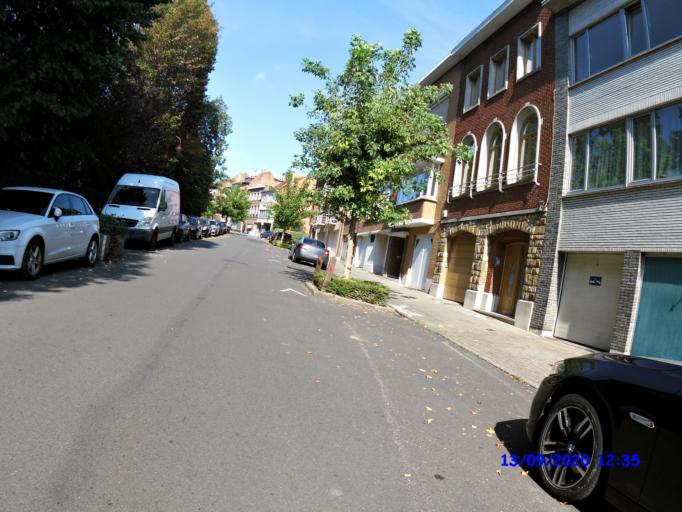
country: BE
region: Flanders
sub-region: Provincie Vlaams-Brabant
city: Wemmel
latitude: 50.8649
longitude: 4.3033
